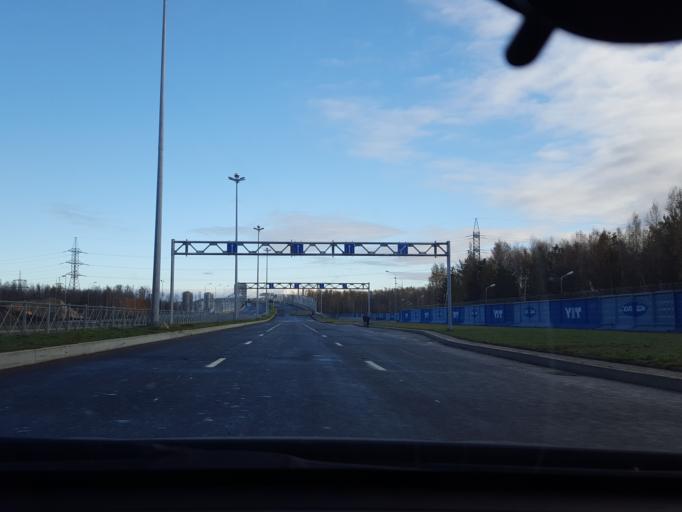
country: RU
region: St.-Petersburg
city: Pargolovo
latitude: 60.0595
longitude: 30.2729
